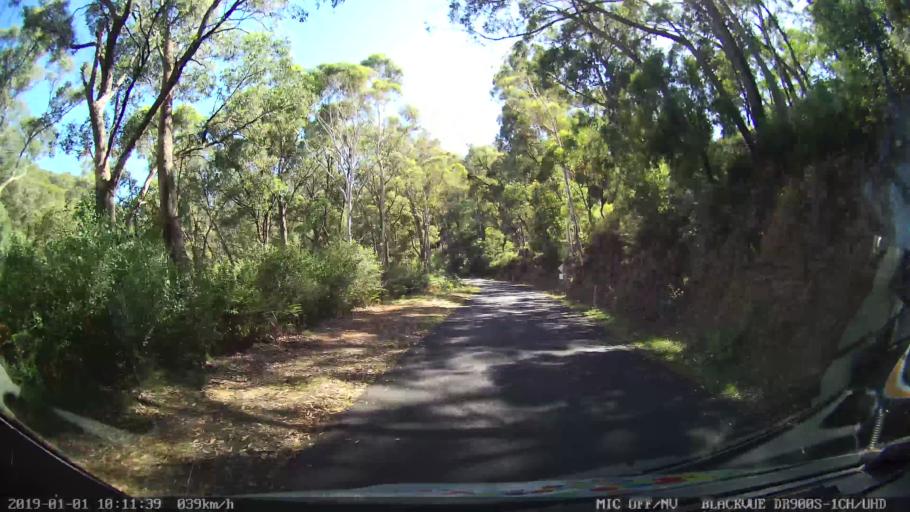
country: AU
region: New South Wales
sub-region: Snowy River
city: Jindabyne
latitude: -36.1360
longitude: 148.1557
